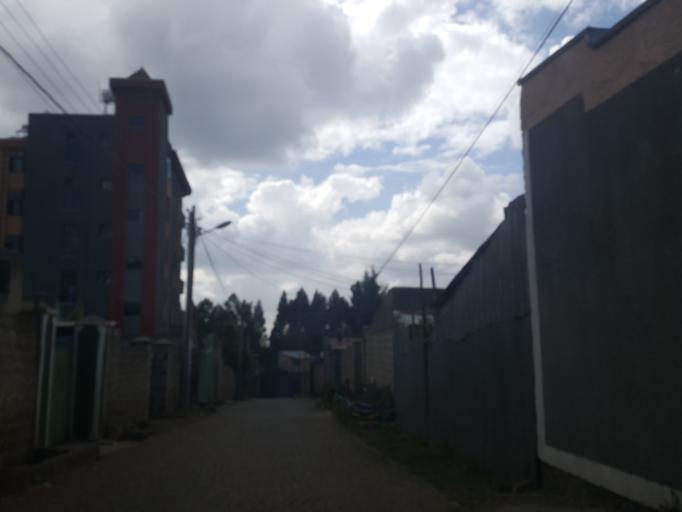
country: ET
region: Adis Abeba
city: Addis Ababa
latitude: 9.0657
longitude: 38.7168
